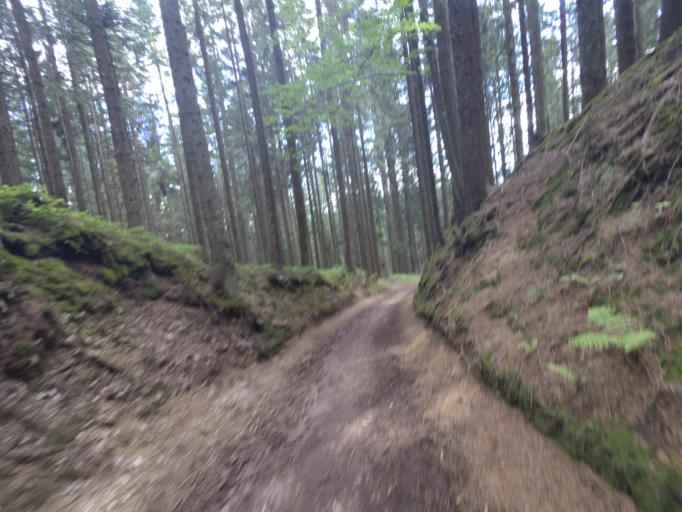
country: AT
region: Salzburg
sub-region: Politischer Bezirk Zell am See
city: Leogang
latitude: 47.4541
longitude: 12.7722
